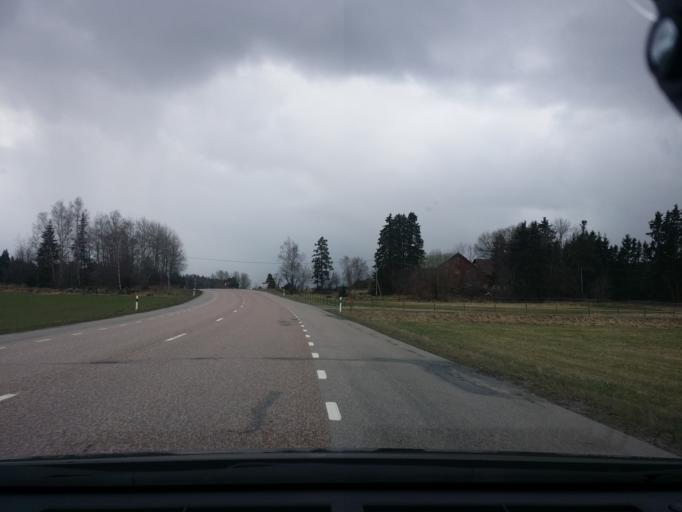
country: SE
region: Uppsala
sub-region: Enkopings Kommun
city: Irsta
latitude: 59.7242
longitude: 16.9592
